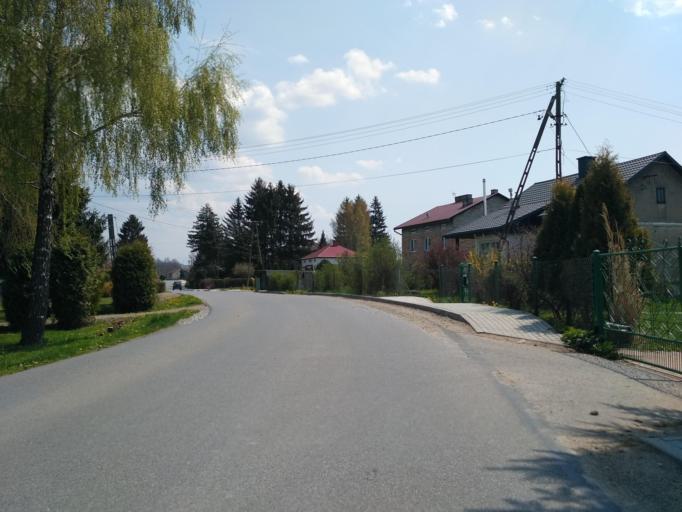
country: PL
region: Subcarpathian Voivodeship
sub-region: Powiat jasielski
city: Tarnowiec
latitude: 49.7391
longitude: 21.5364
